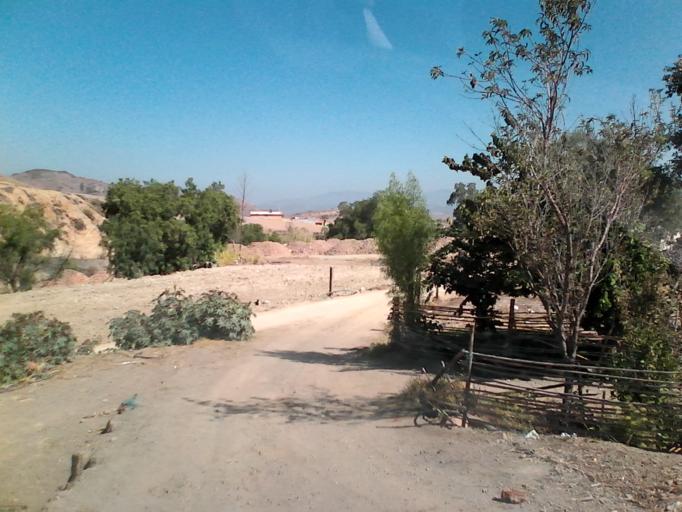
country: CO
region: Boyaca
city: Sachica
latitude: 5.5691
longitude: -73.5484
